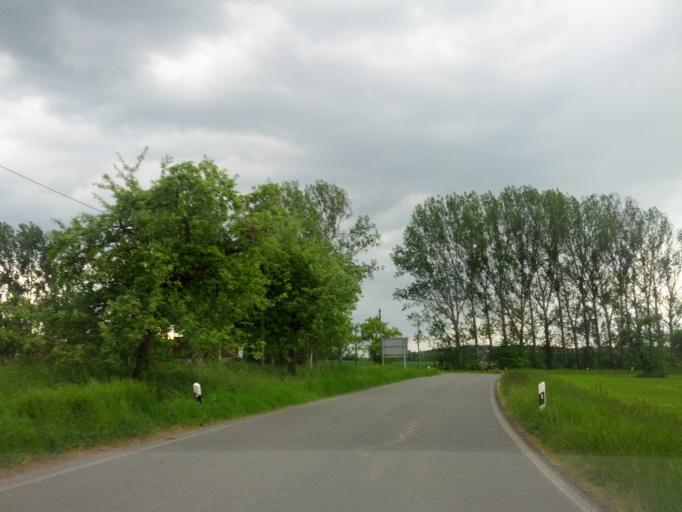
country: DE
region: Thuringia
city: Friedrichswerth
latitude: 50.9891
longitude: 10.5419
